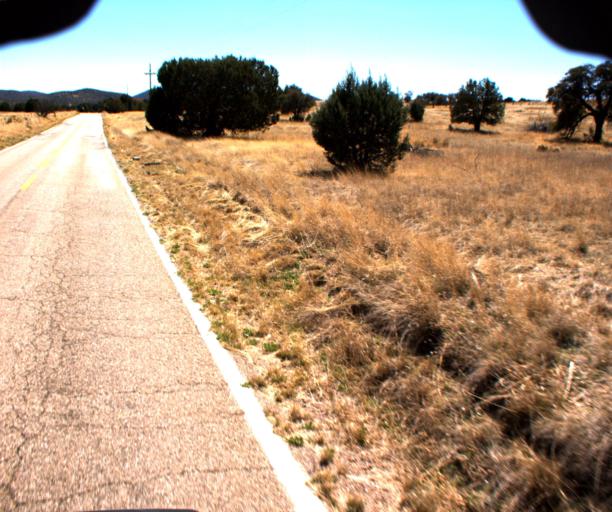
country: US
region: Arizona
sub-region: Cochise County
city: Huachuca City
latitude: 31.5453
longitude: -110.5295
